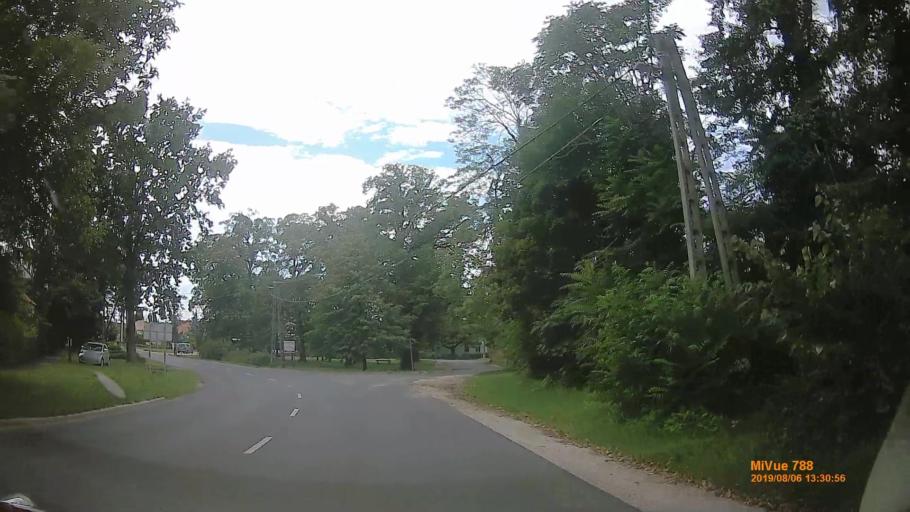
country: HU
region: Vas
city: Gencsapati
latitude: 47.2636
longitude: 16.6028
